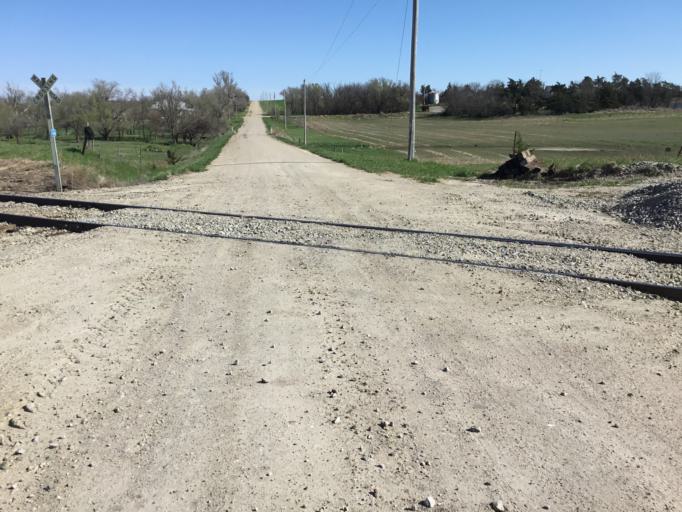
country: US
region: Kansas
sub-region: Norton County
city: Norton
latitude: 39.8488
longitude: -99.6090
